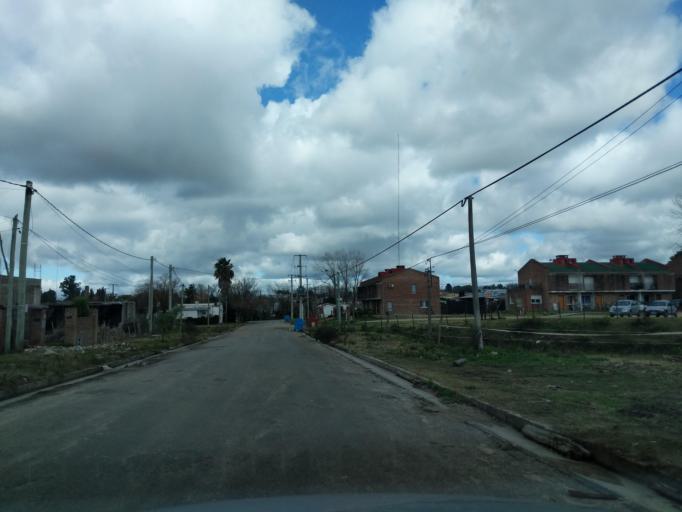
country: UY
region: Florida
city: Florida
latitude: -34.0912
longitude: -56.2340
